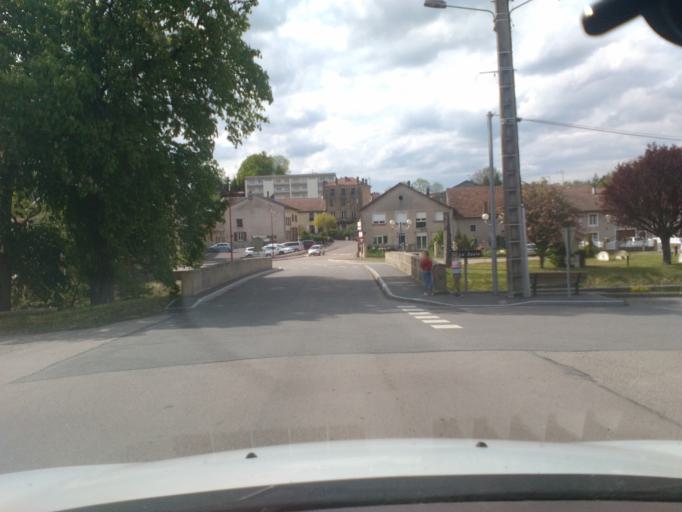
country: FR
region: Lorraine
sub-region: Departement des Vosges
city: Mirecourt
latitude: 48.2653
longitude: 6.1431
